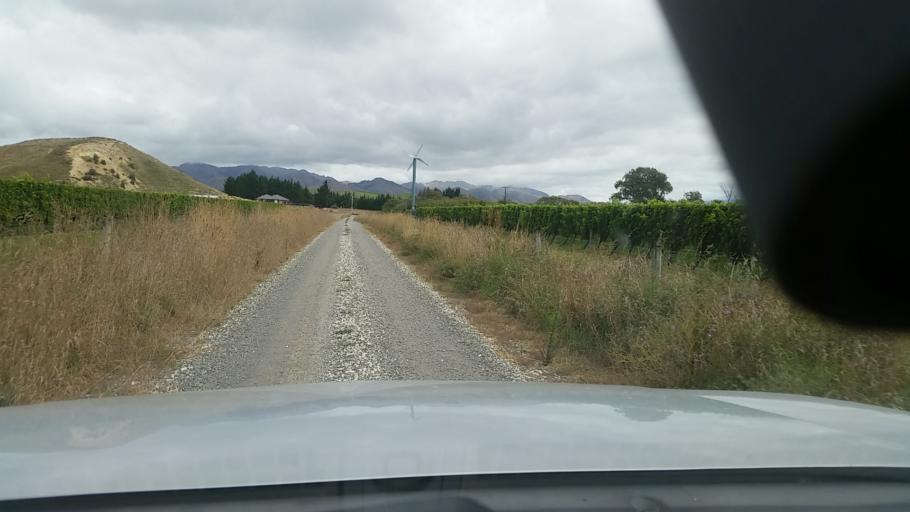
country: NZ
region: Marlborough
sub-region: Marlborough District
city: Blenheim
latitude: -41.6964
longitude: 174.1230
